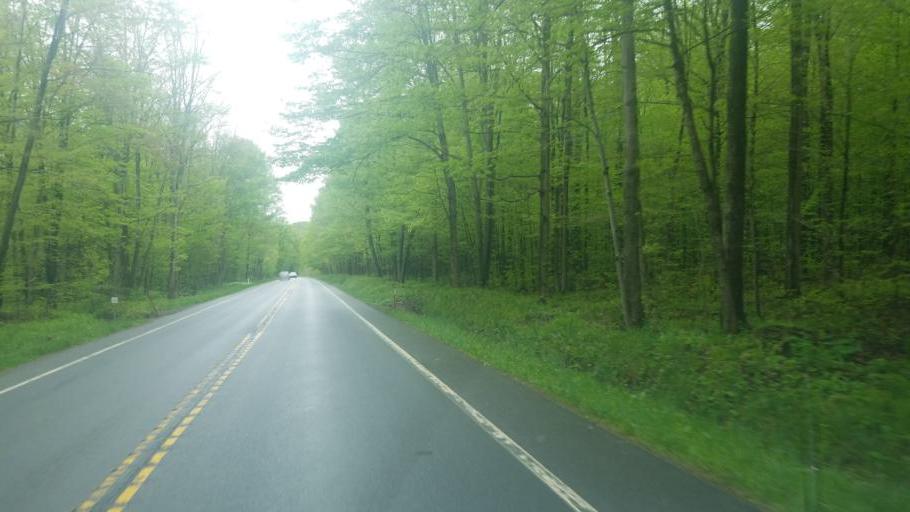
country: US
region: Pennsylvania
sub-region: McKean County
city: Kane
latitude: 41.6062
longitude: -78.8416
